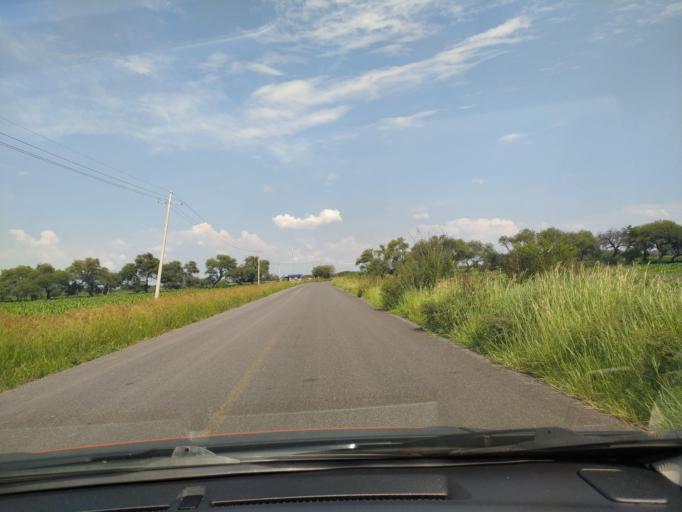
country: MX
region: Guanajuato
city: San Roque
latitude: 20.9539
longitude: -101.8882
